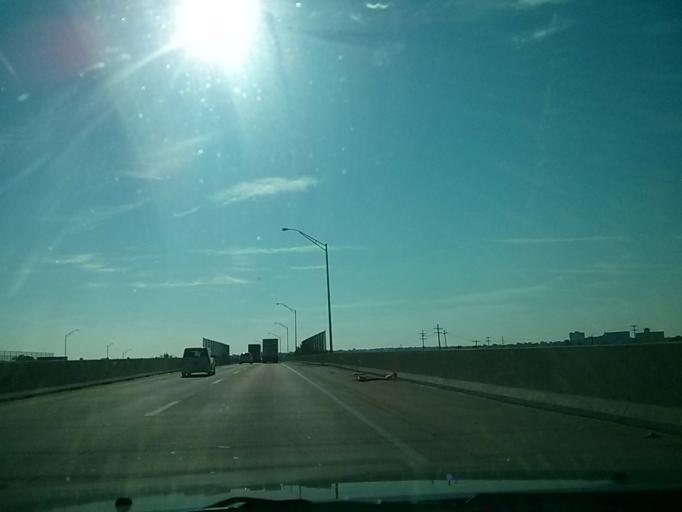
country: US
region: Oklahoma
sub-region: Tulsa County
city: Tulsa
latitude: 36.1599
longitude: -95.9836
